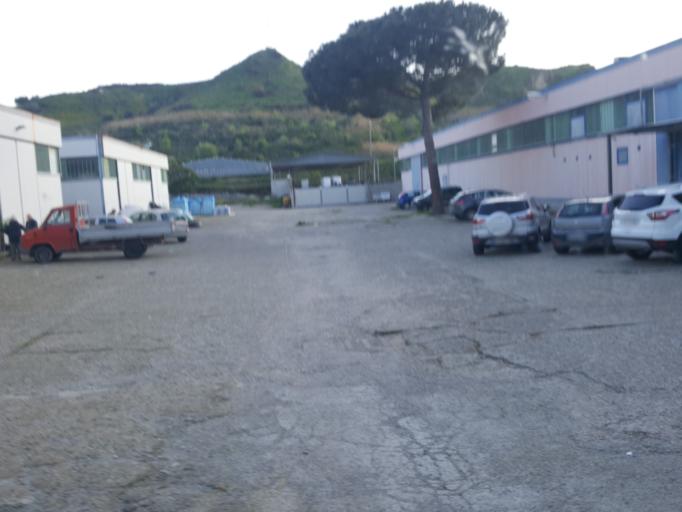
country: IT
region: Calabria
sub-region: Provincia di Catanzaro
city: Roccelletta
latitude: 38.8145
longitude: 16.5842
